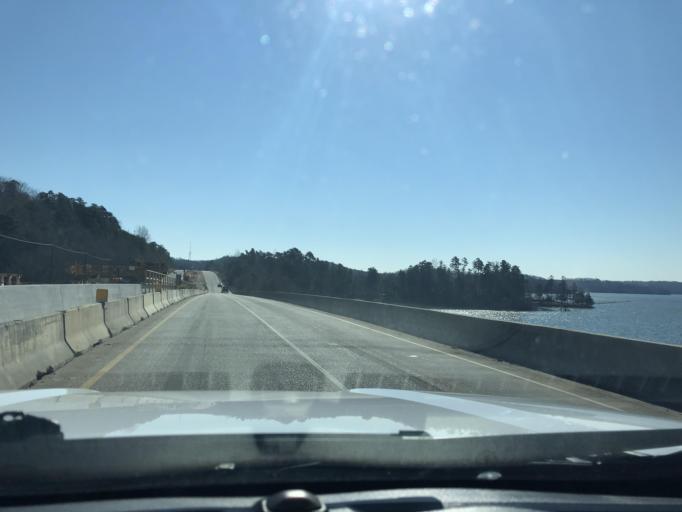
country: US
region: Georgia
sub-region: Hall County
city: Gainesville
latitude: 34.3221
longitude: -83.8800
